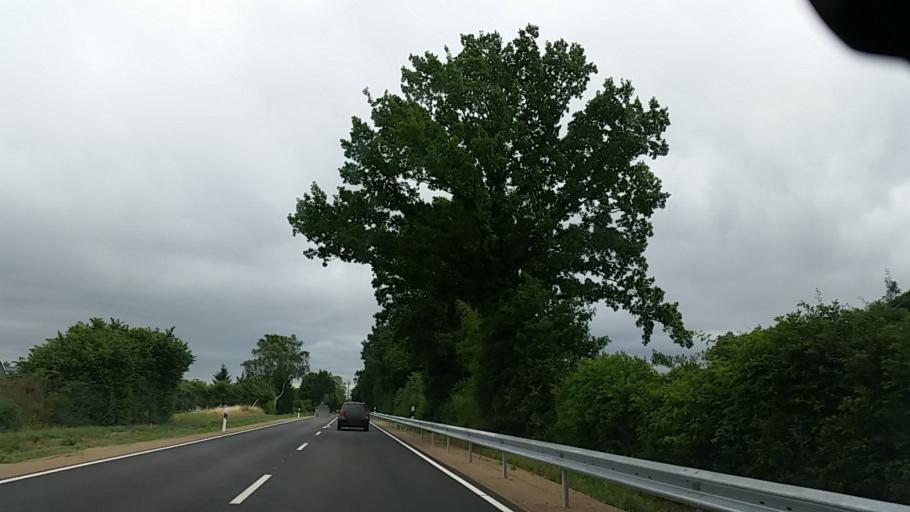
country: DE
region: Schleswig-Holstein
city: Gammelby
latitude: 54.4884
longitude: 9.7946
